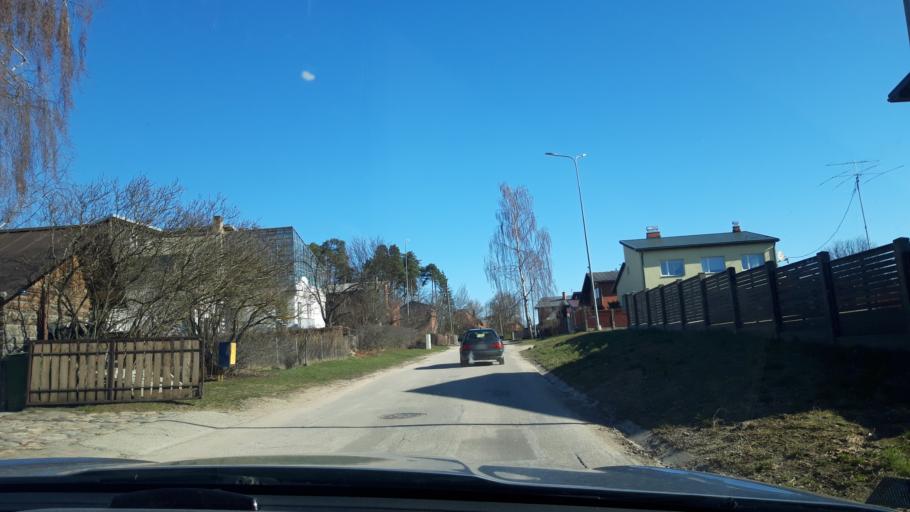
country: LV
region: Valmieras Rajons
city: Valmiera
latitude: 57.5463
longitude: 25.4546
